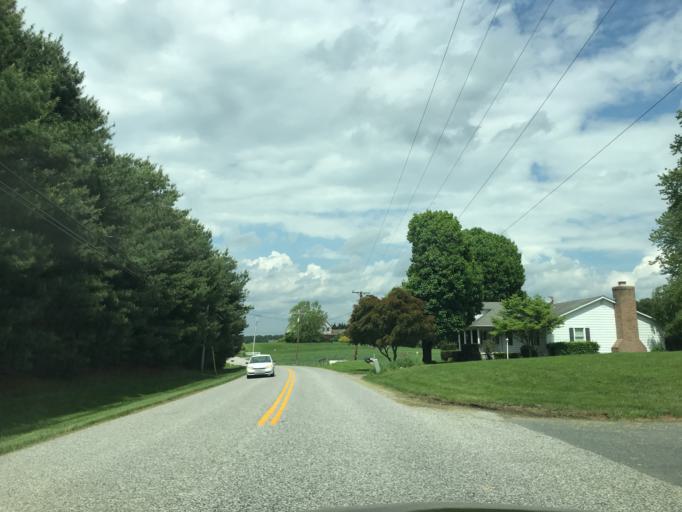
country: US
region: Maryland
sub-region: Harford County
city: Bel Air North
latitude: 39.6061
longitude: -76.3688
